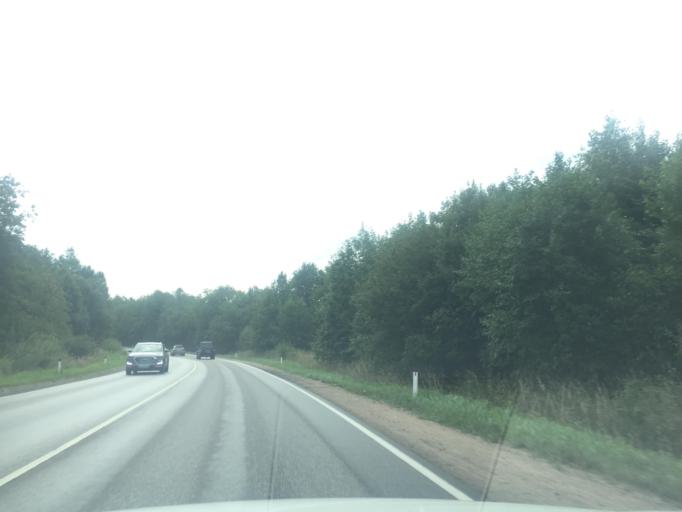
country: RU
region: Leningrad
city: Rozhdestveno
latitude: 59.3455
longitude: 30.0002
